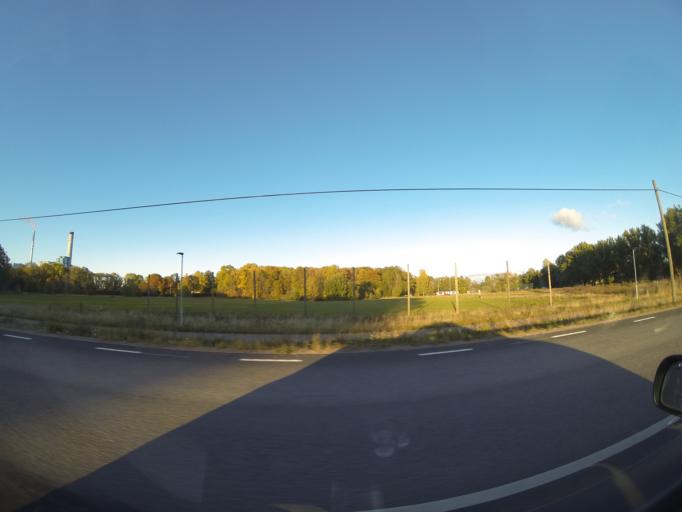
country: SE
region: Vaestmanland
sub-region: Vasteras
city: Vasteras
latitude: 59.5807
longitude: 16.5149
